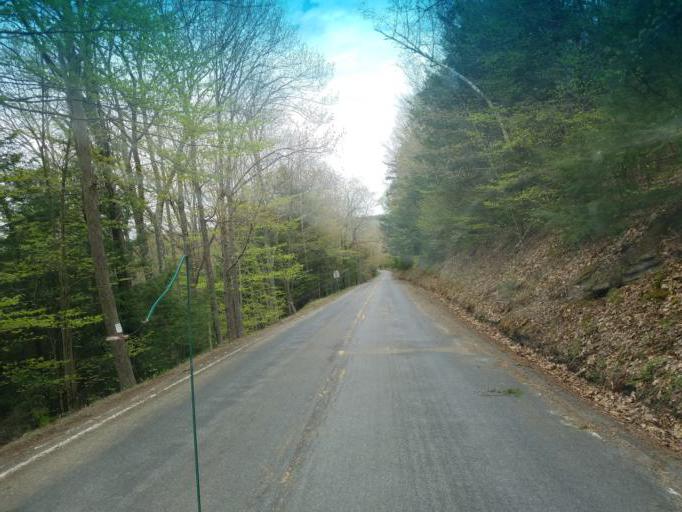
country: US
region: Pennsylvania
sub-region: Tioga County
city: Wellsboro
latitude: 41.6989
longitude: -77.4500
